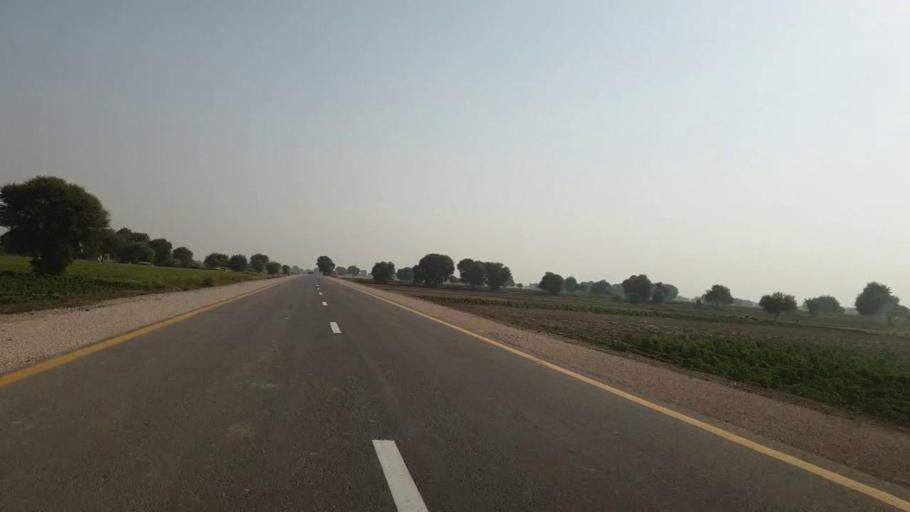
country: PK
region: Sindh
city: Bhan
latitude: 26.5301
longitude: 67.7890
